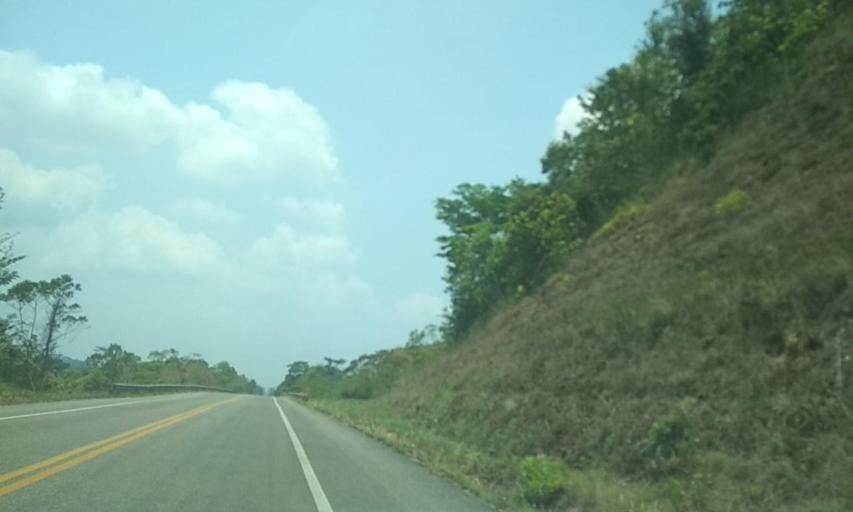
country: MX
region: Tabasco
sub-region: Huimanguillo
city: Francisco Rueda
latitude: 17.6575
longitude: -93.8485
